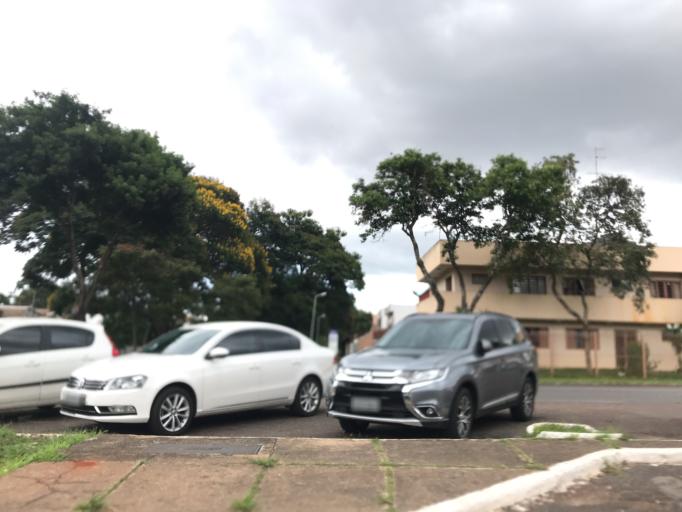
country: BR
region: Federal District
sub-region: Brasilia
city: Brasilia
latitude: -15.8190
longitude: -47.9152
